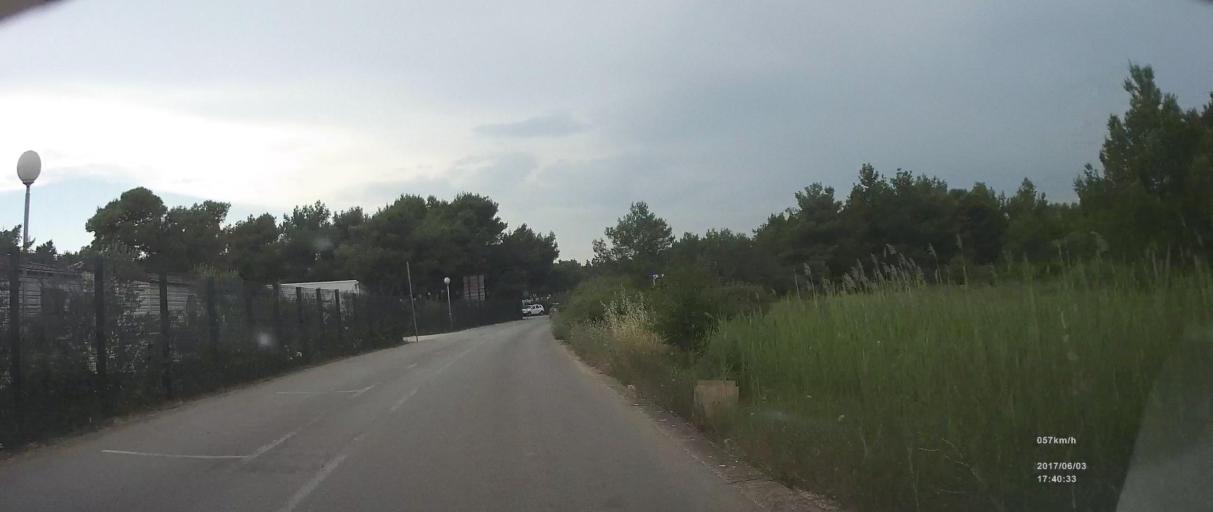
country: HR
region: Sibensko-Kniniska
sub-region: Grad Sibenik
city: Sibenik
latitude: 43.6990
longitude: 15.8806
